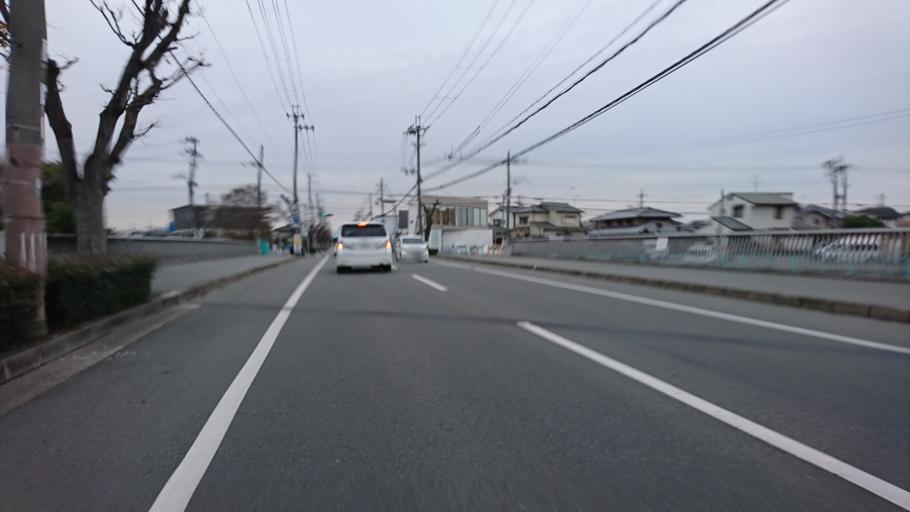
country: JP
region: Hyogo
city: Kakogawacho-honmachi
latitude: 34.7641
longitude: 134.8226
